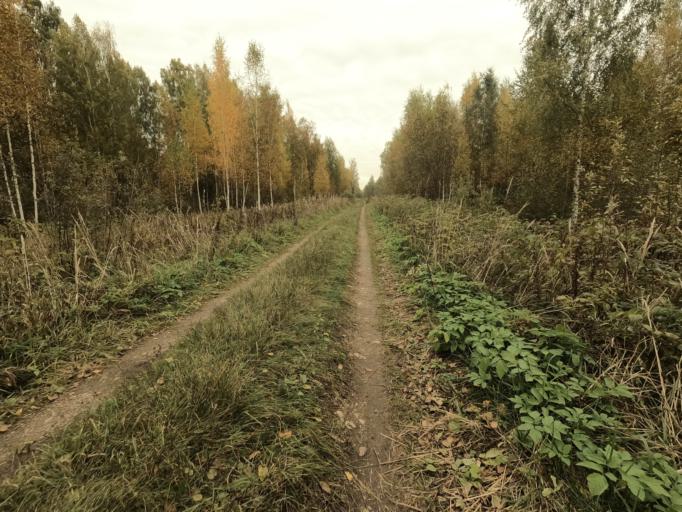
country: RU
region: Novgorod
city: Pankovka
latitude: 58.8674
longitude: 30.9345
